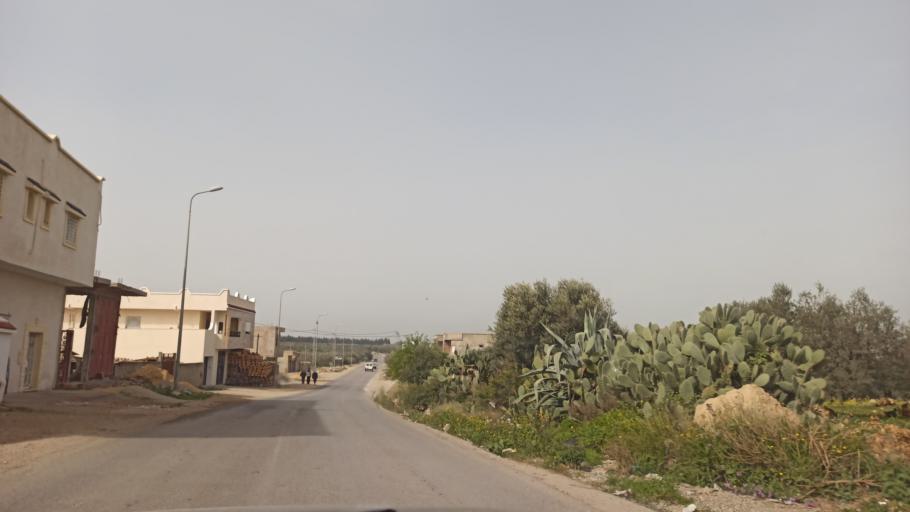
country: TN
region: Zaghwan
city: Zaghouan
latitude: 36.4177
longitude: 10.1192
